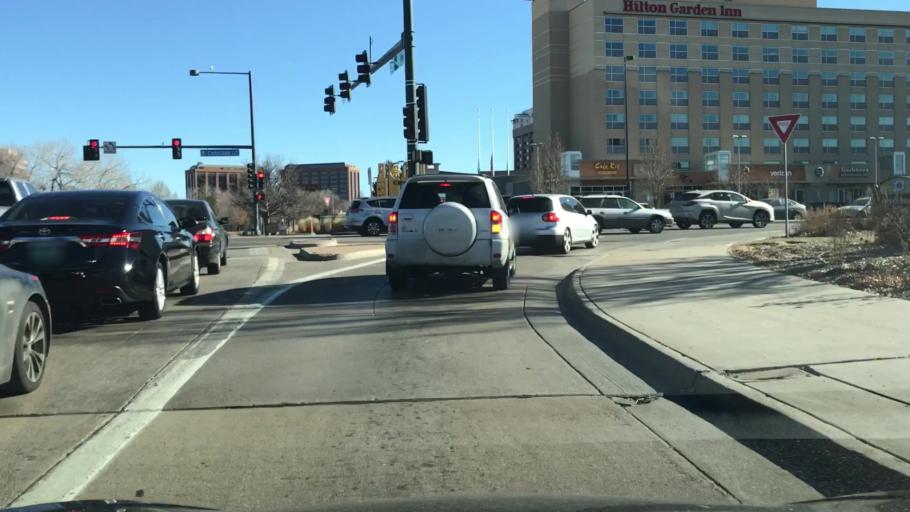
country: US
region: Colorado
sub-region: Arapahoe County
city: Glendale
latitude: 39.7060
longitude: -104.9412
